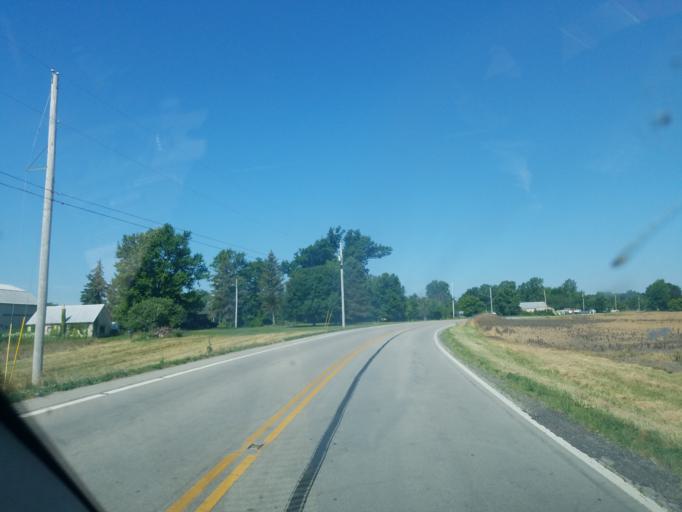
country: US
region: Ohio
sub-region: Logan County
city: Russells Point
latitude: 40.4636
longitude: -83.8288
